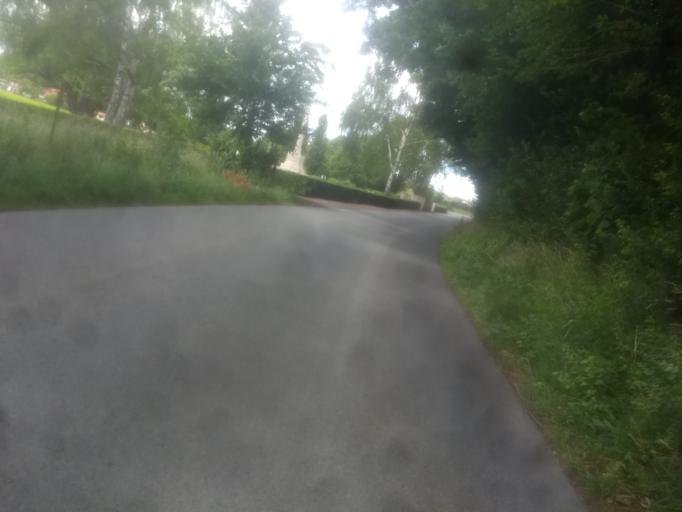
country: FR
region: Nord-Pas-de-Calais
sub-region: Departement du Pas-de-Calais
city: Mont-Saint-Eloi
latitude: 50.3419
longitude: 2.6871
